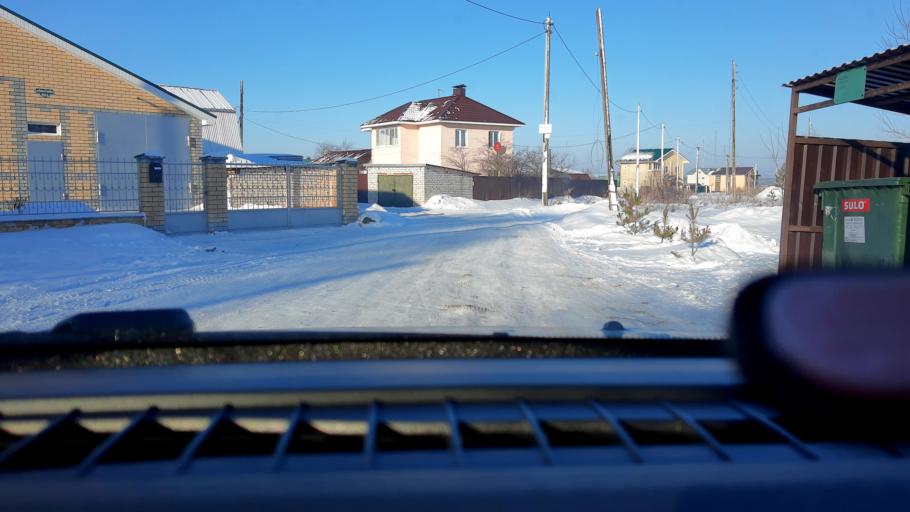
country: RU
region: Nizjnij Novgorod
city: Burevestnik
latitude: 56.1415
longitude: 43.9227
